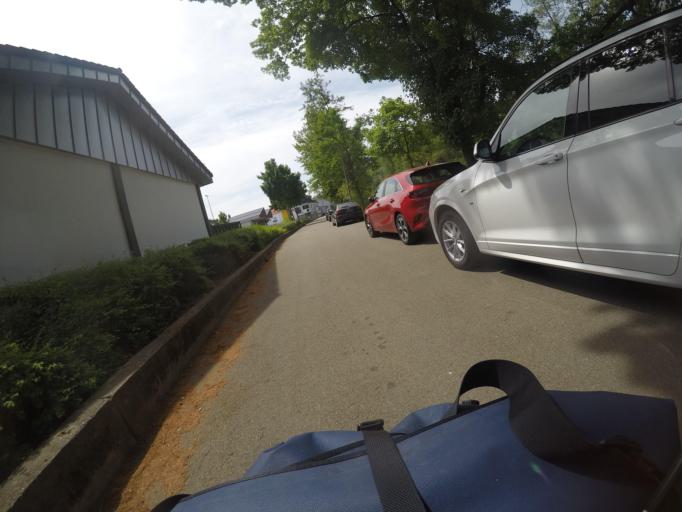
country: DE
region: Baden-Wuerttemberg
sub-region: Karlsruhe Region
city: Nagold
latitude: 48.5593
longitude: 8.7238
